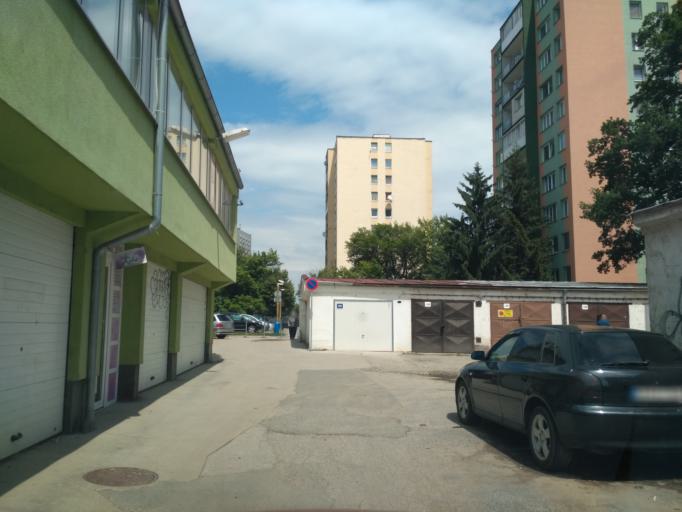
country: SK
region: Kosicky
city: Kosice
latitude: 48.7186
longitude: 21.2387
